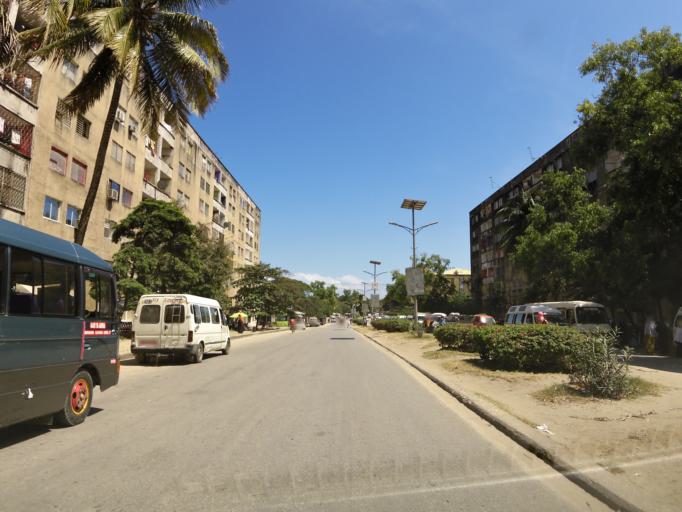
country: TZ
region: Zanzibar Urban/West
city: Zanzibar
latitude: -6.1649
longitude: 39.1965
